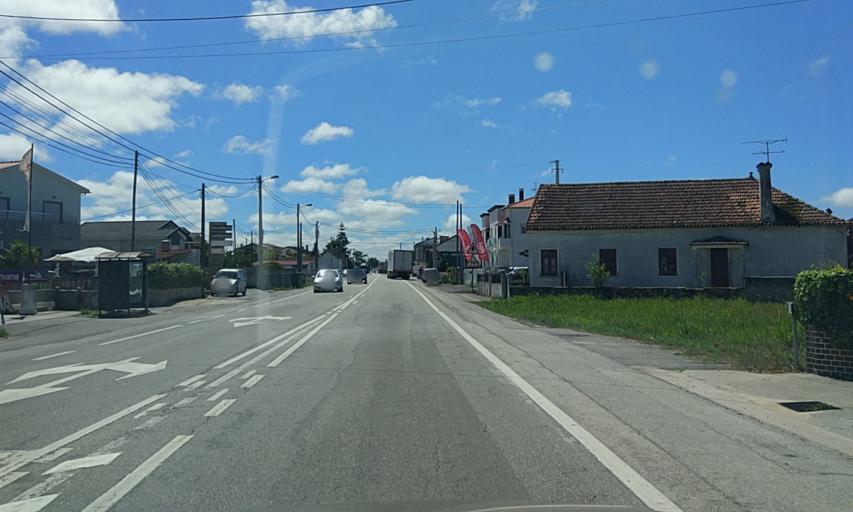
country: PT
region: Coimbra
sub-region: Mira
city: Mira
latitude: 40.4760
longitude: -8.6958
